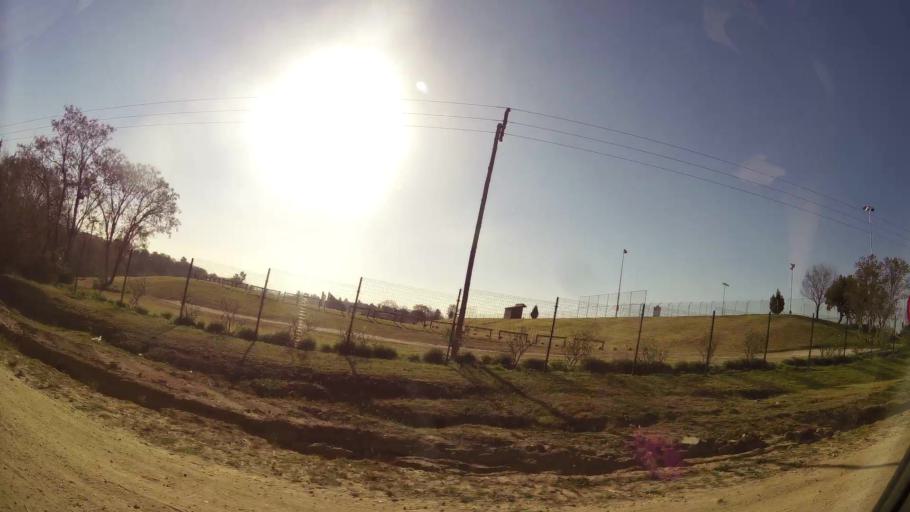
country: ZA
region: Gauteng
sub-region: City of Johannesburg Metropolitan Municipality
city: Diepsloot
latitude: -25.9528
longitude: 27.9627
